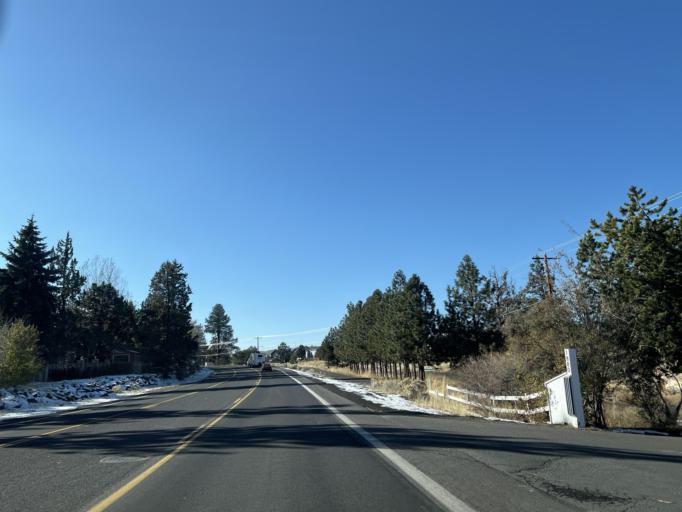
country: US
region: Oregon
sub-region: Deschutes County
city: Bend
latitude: 44.0833
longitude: -121.2767
